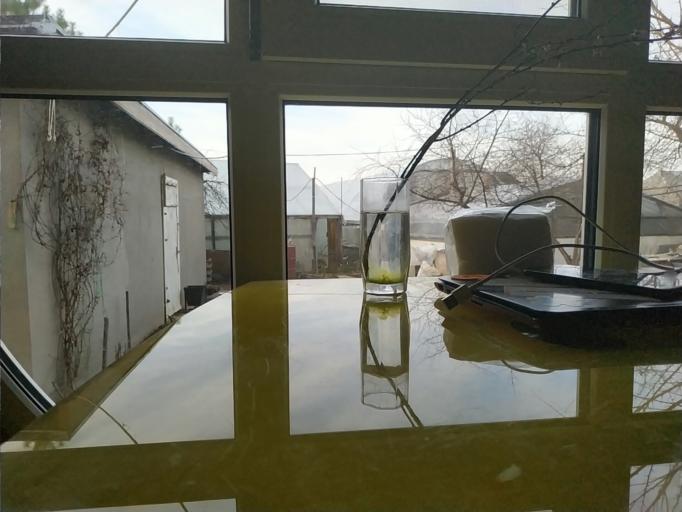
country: RU
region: Republic of Karelia
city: Suoyarvi
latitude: 61.8448
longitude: 32.2806
